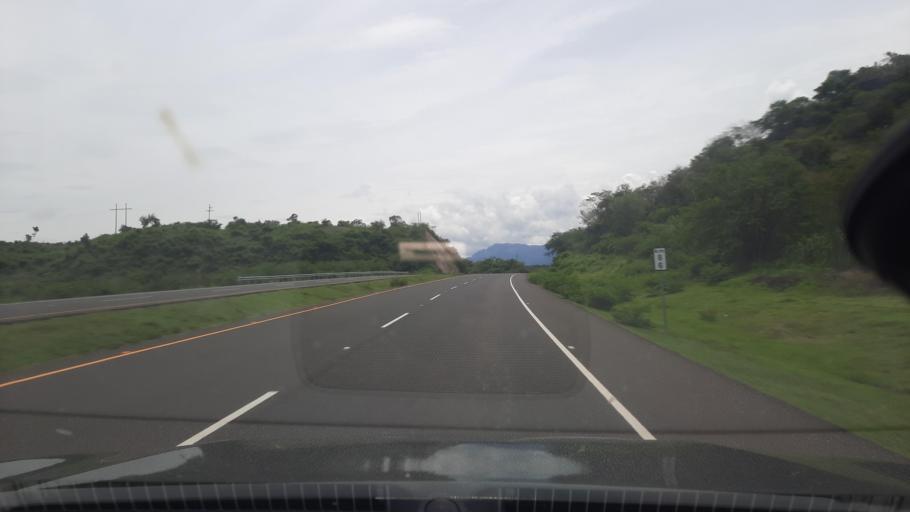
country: HN
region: Valle
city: Aramecina
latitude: 13.6799
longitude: -87.7298
